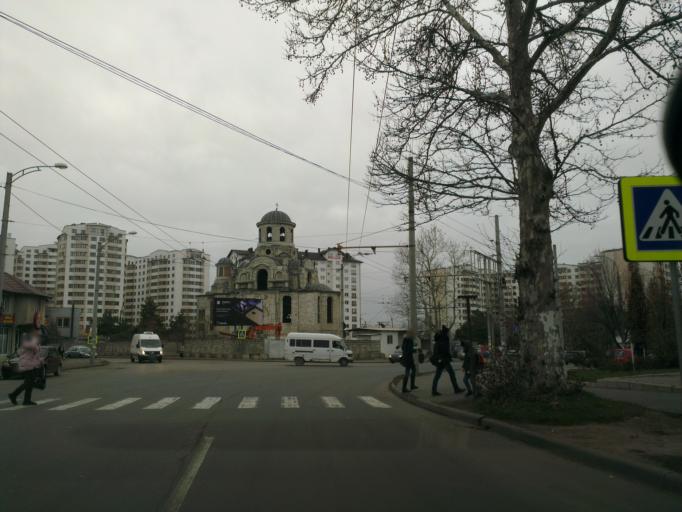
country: MD
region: Chisinau
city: Chisinau
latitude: 46.9858
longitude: 28.8449
